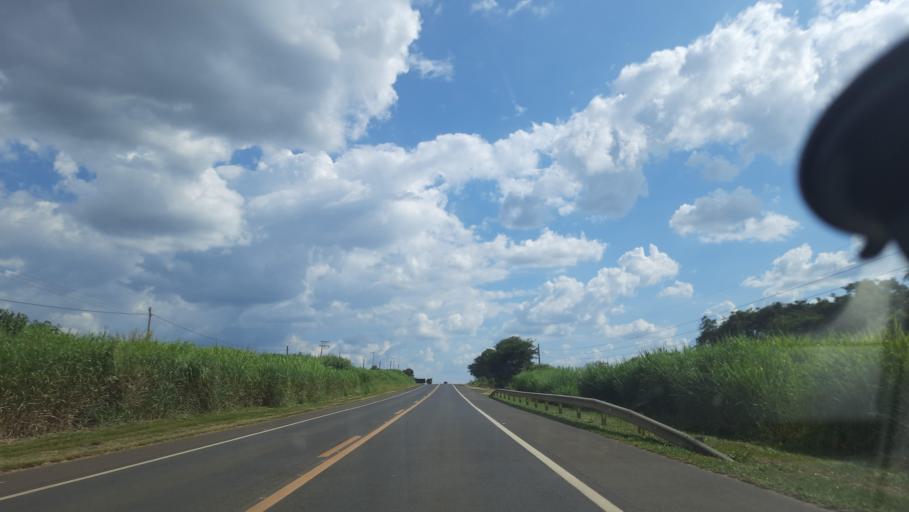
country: BR
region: Sao Paulo
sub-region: Sao Jose Do Rio Pardo
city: Sao Jose do Rio Pardo
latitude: -21.6726
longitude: -46.9232
